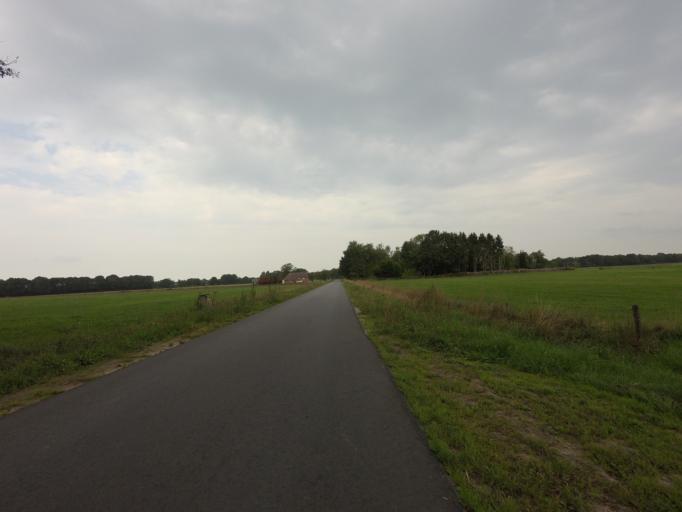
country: NL
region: Drenthe
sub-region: Gemeente Tynaarlo
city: Vries
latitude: 53.0602
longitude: 6.5859
